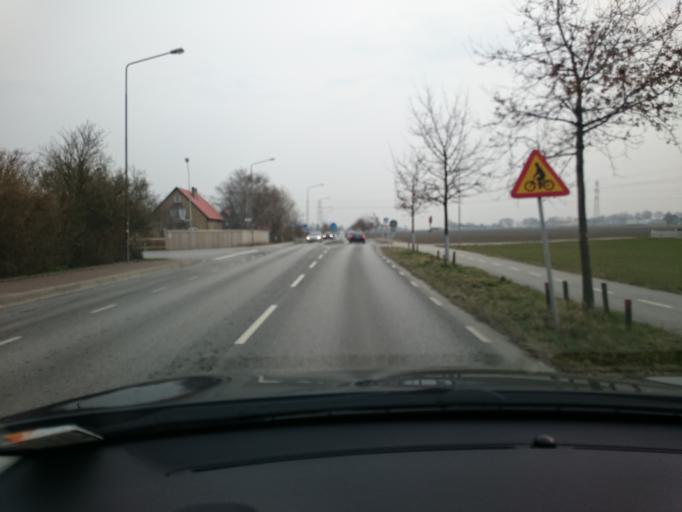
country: SE
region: Skane
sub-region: Staffanstorps Kommun
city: Hjaerup
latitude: 55.6666
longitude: 13.1539
